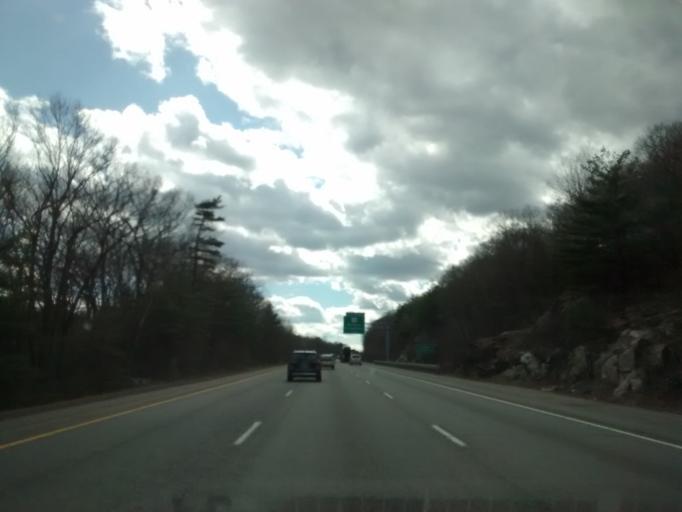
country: US
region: Massachusetts
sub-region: Worcester County
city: Shrewsbury
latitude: 42.3288
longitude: -71.6966
